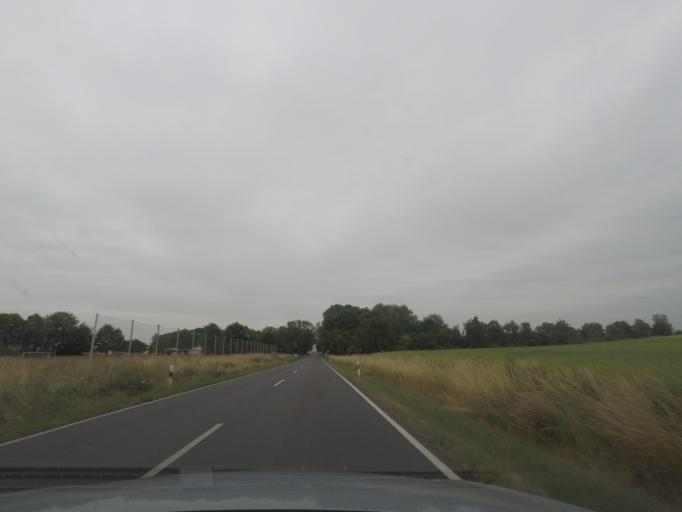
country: DE
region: Saxony-Anhalt
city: Seehausen
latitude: 52.0631
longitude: 11.2860
